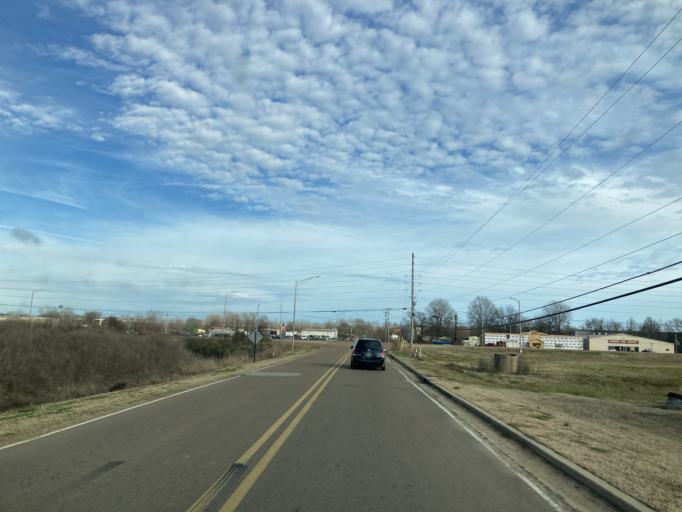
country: US
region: Mississippi
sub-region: Humphreys County
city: Belzoni
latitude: 33.1676
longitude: -90.5002
